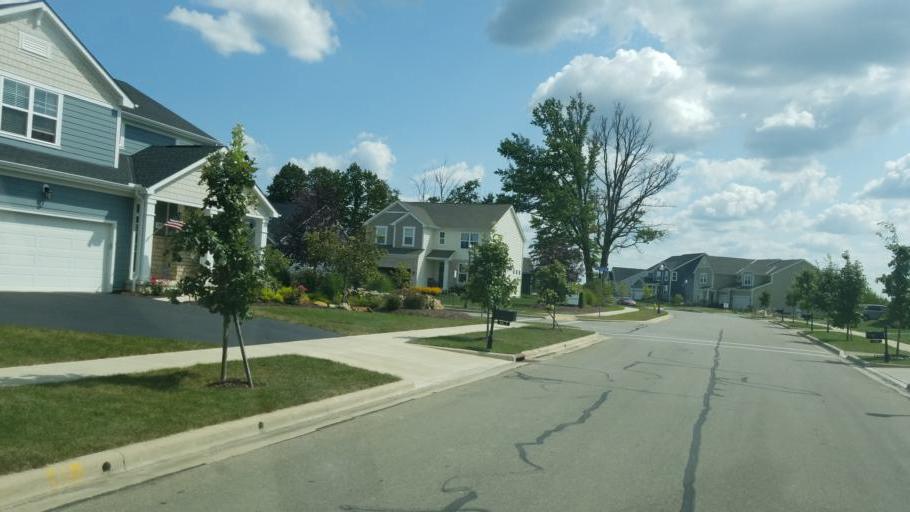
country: US
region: Ohio
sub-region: Delaware County
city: Lewis Center
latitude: 40.2474
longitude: -83.0241
